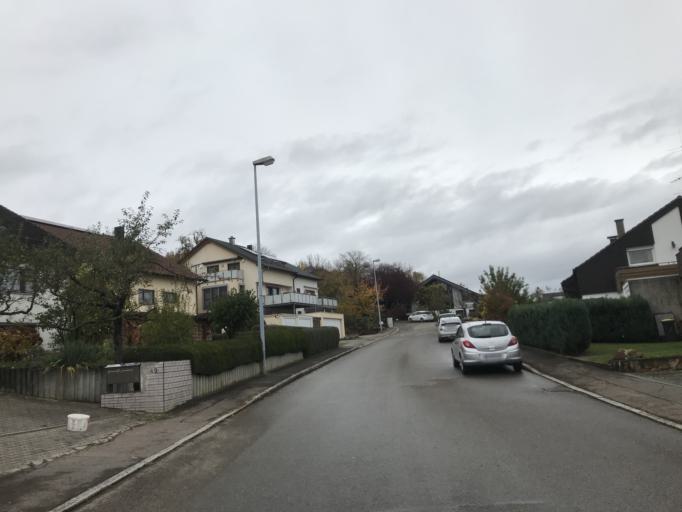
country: DE
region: Baden-Wuerttemberg
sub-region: Regierungsbezirk Stuttgart
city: Unterensingen
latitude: 48.6471
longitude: 9.3486
